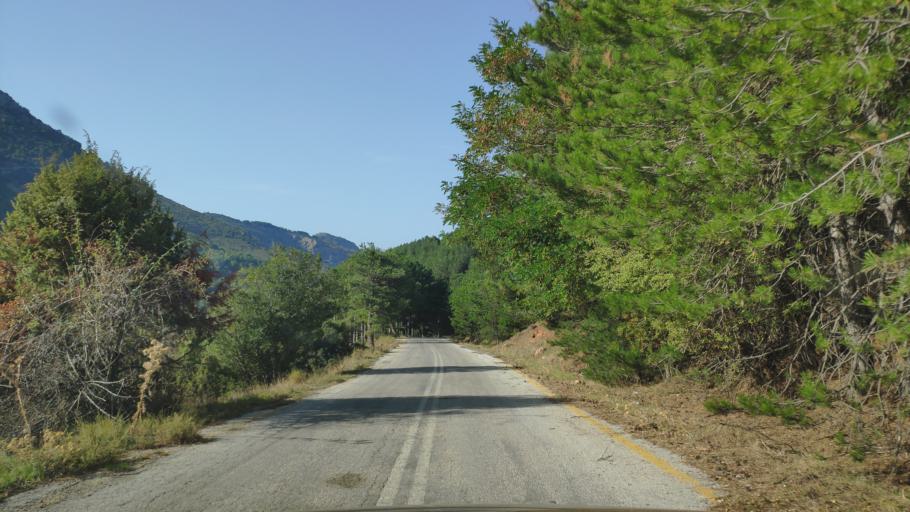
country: GR
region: West Greece
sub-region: Nomos Achaias
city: Aiyira
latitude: 38.0503
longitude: 22.3842
